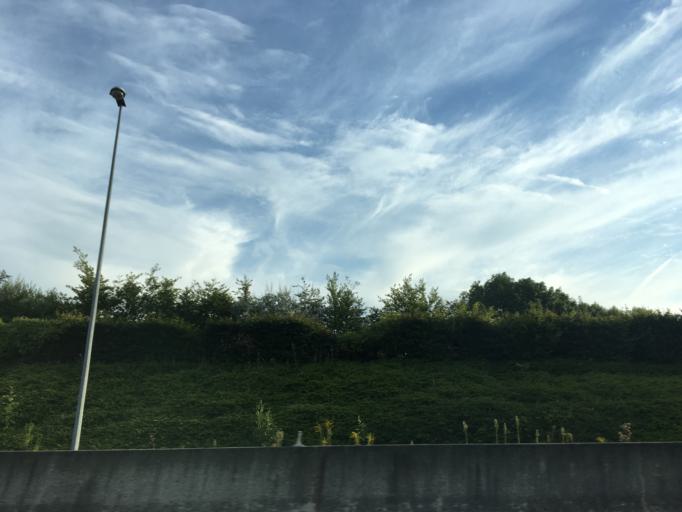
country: FR
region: Ile-de-France
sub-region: Departement des Yvelines
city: Chambourcy
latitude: 48.9166
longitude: 2.0204
